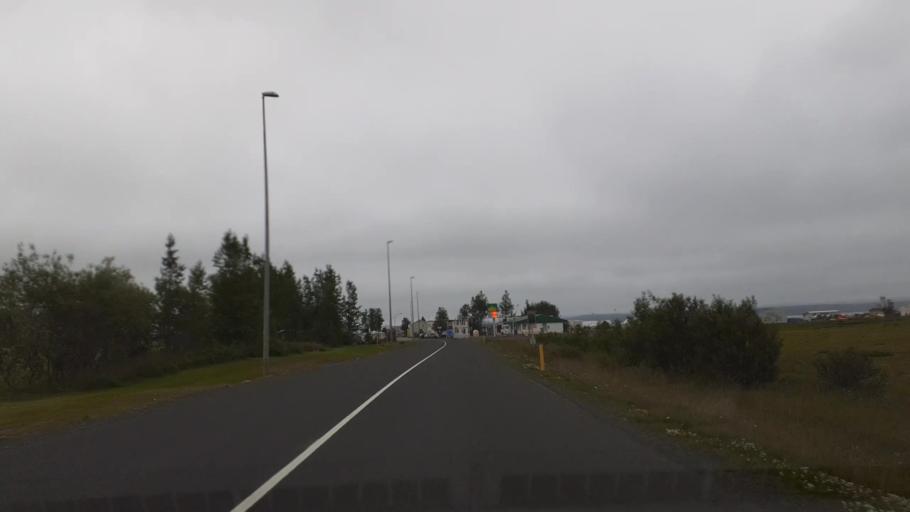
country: IS
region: Northeast
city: Dalvik
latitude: 65.9660
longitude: -18.5319
